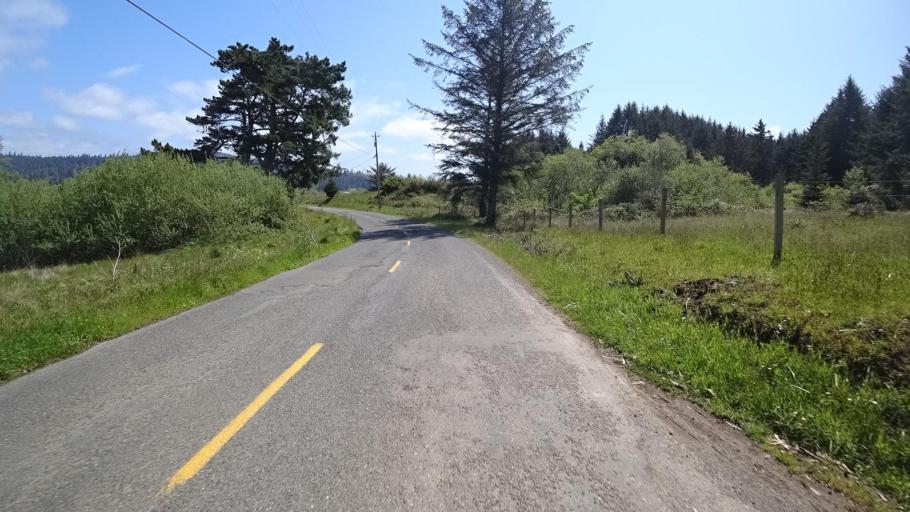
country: US
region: California
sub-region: Humboldt County
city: Humboldt Hill
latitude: 40.6720
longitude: -124.2146
